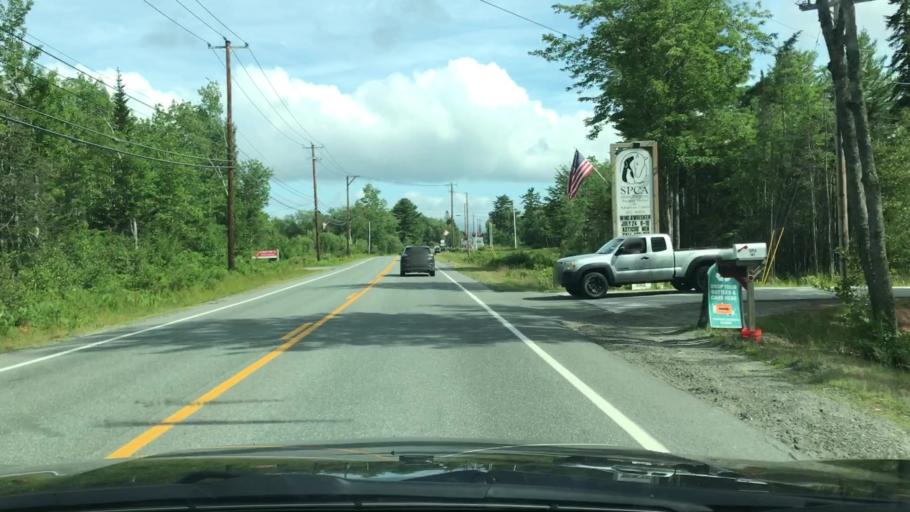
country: US
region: Maine
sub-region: Hancock County
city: Ellsworth
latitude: 44.5020
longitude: -68.3839
